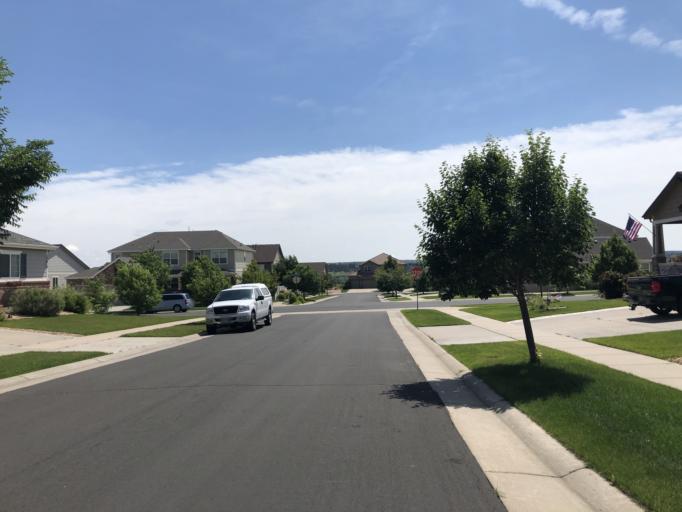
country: US
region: Colorado
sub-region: Douglas County
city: Parker
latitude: 39.4973
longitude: -104.7828
